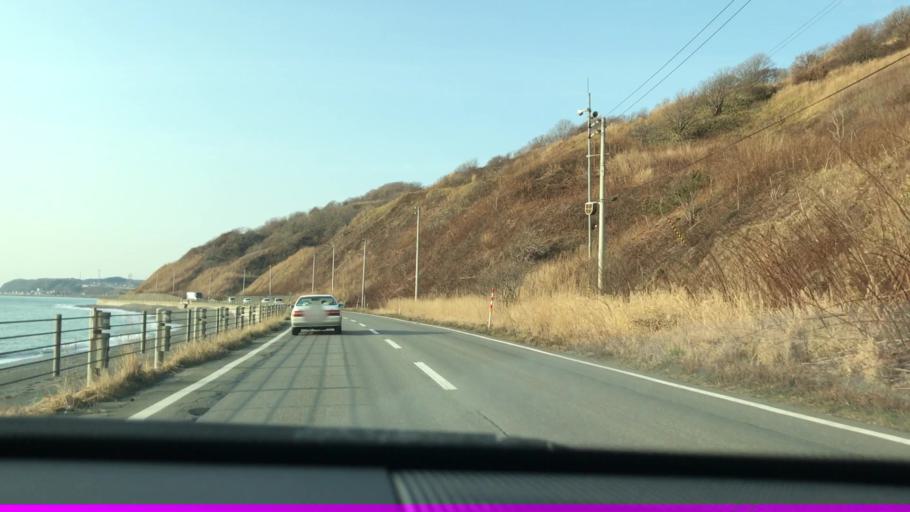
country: JP
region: Hokkaido
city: Shizunai-furukawacho
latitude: 42.2351
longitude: 142.6001
